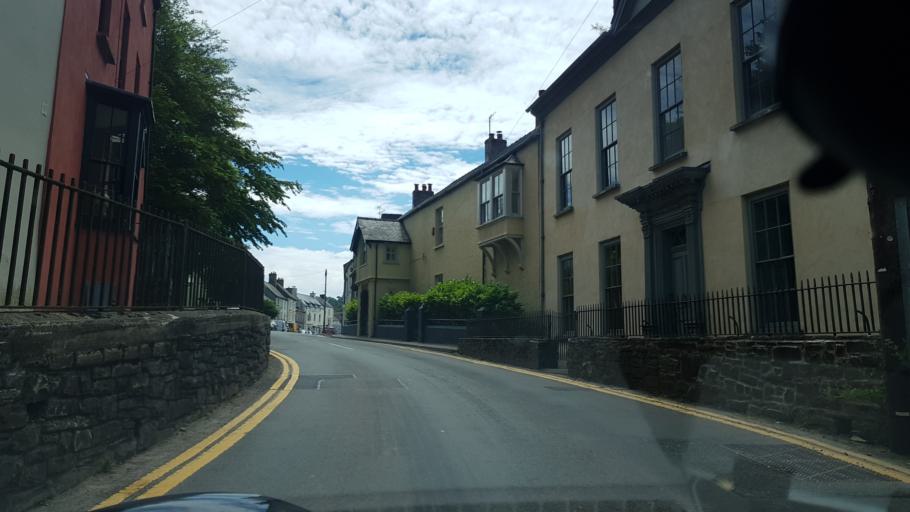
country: GB
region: Wales
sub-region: Carmarthenshire
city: Saint Clears
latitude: 51.7727
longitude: -4.4631
